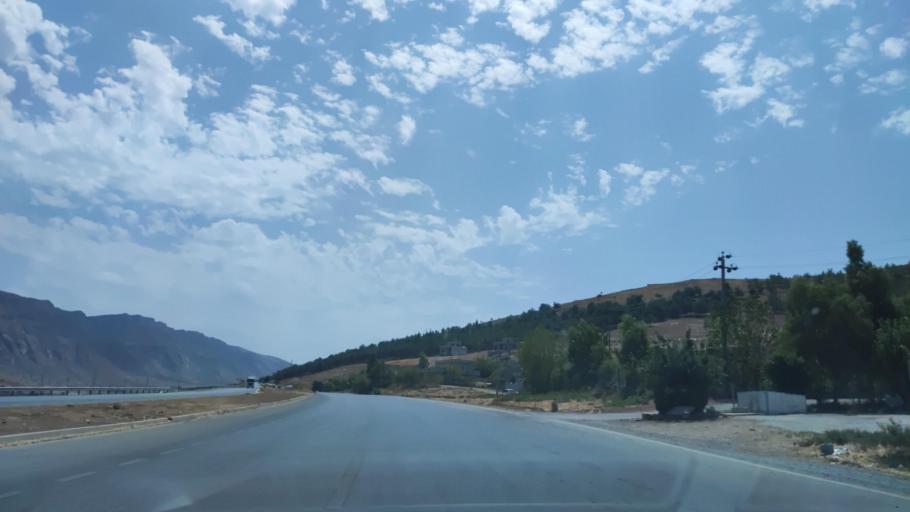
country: IQ
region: Arbil
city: Shaqlawah
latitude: 36.4934
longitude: 44.3689
